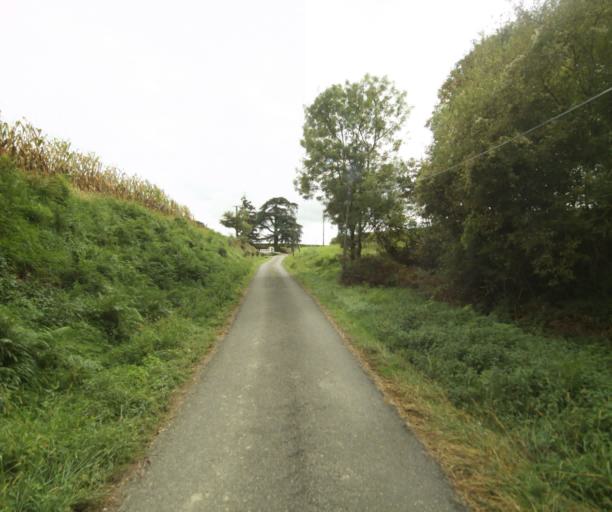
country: FR
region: Midi-Pyrenees
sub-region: Departement du Gers
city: Nogaro
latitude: 43.8337
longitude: -0.0079
